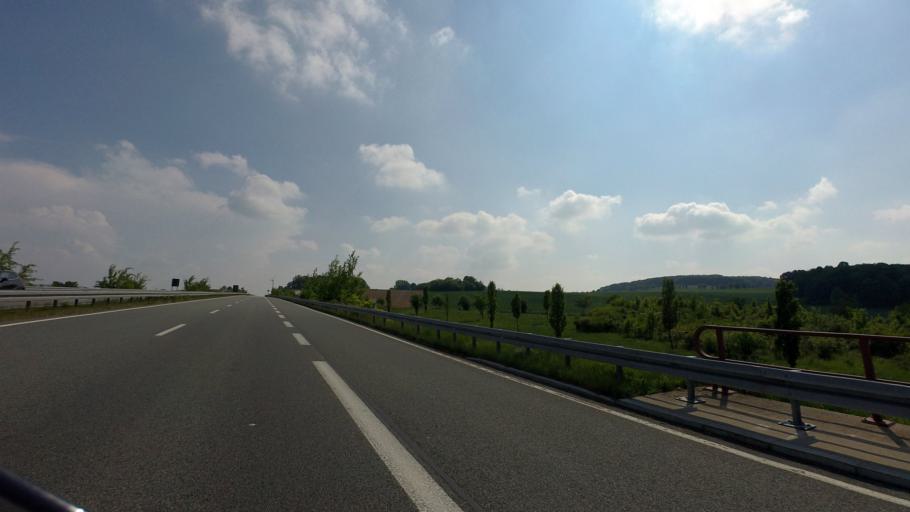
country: DE
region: Saxony
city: Weissenberg
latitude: 51.1498
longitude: 14.6542
